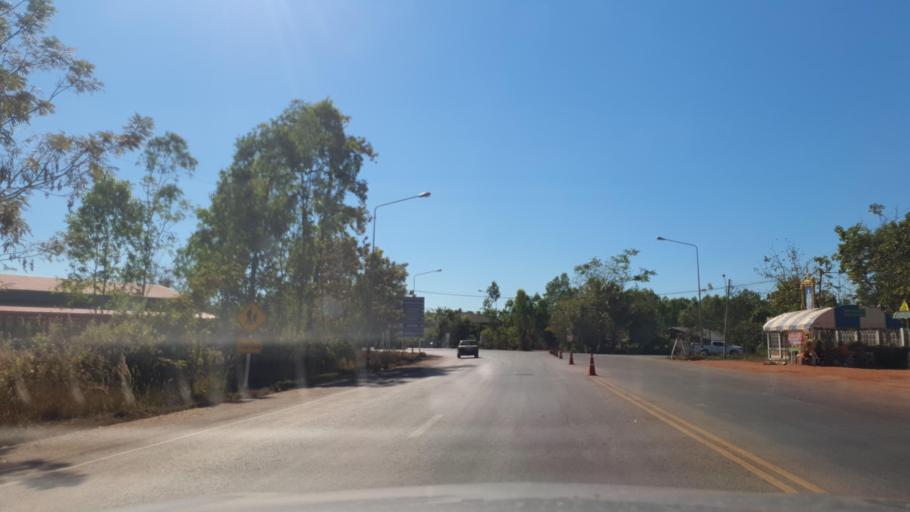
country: TH
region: Nakhon Phanom
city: Si Songkhram
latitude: 17.7664
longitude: 104.2782
